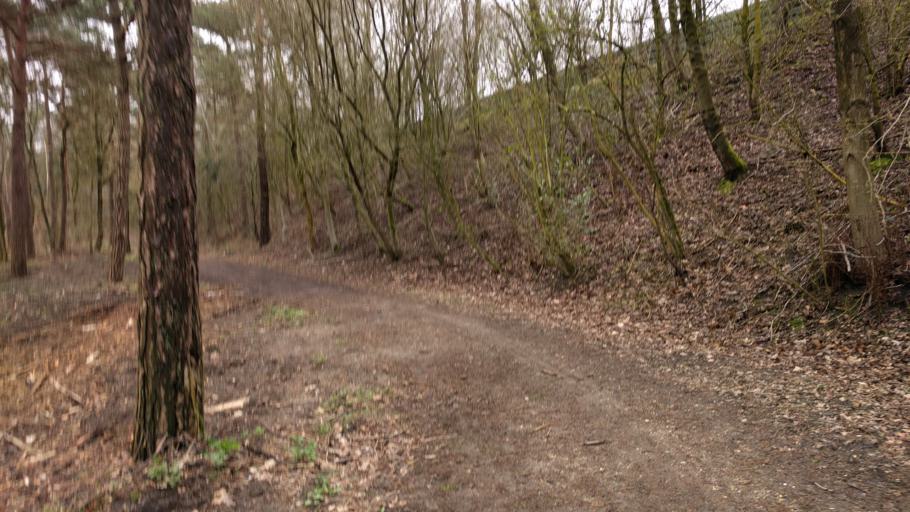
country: NL
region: Gelderland
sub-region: Gemeente Oldebroek
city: Oldebroek
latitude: 52.4391
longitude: 5.9590
